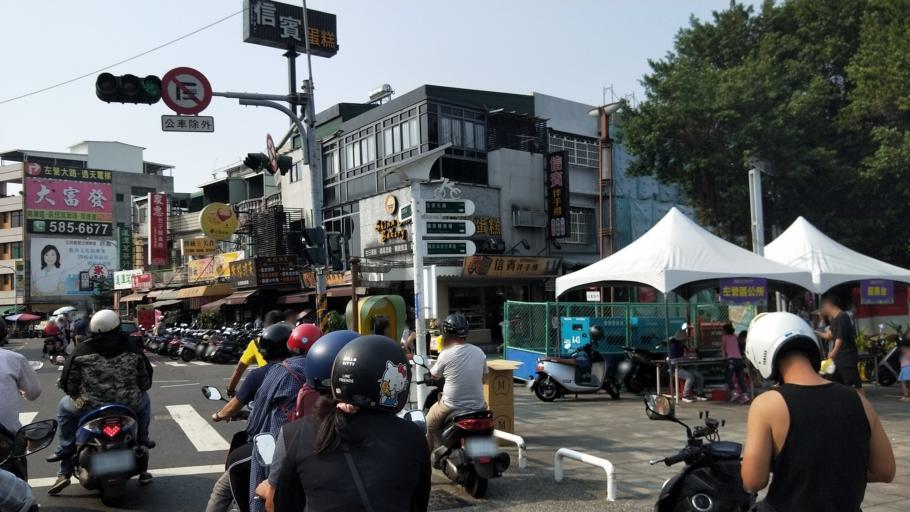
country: TW
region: Kaohsiung
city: Kaohsiung
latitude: 22.6801
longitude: 120.2917
